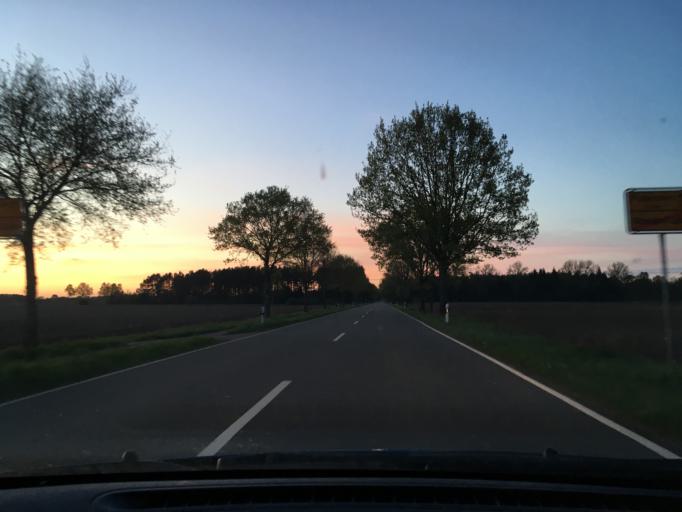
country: DE
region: Lower Saxony
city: Oldendorf
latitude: 53.1614
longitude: 10.2129
